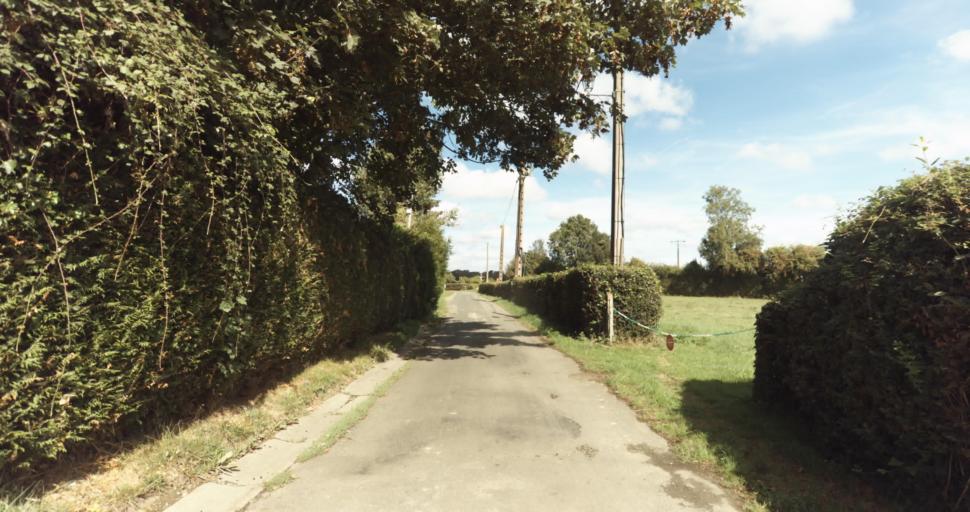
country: FR
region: Lower Normandy
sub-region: Departement du Calvados
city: Orbec
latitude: 48.9419
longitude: 0.3790
